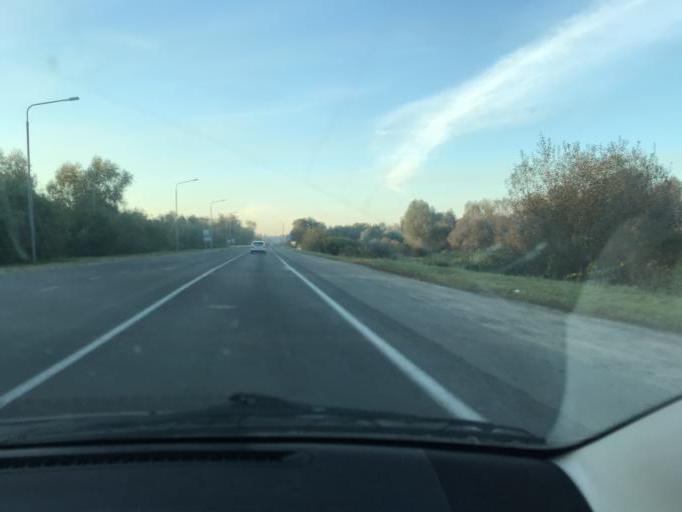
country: BY
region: Brest
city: Pinsk
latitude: 52.1022
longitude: 26.1129
